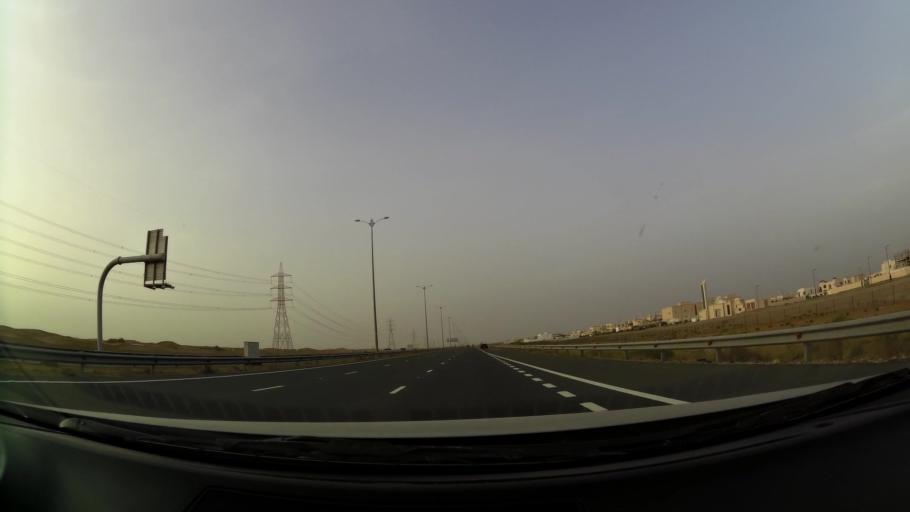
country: OM
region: Al Buraimi
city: Al Buraymi
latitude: 24.3537
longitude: 55.7831
